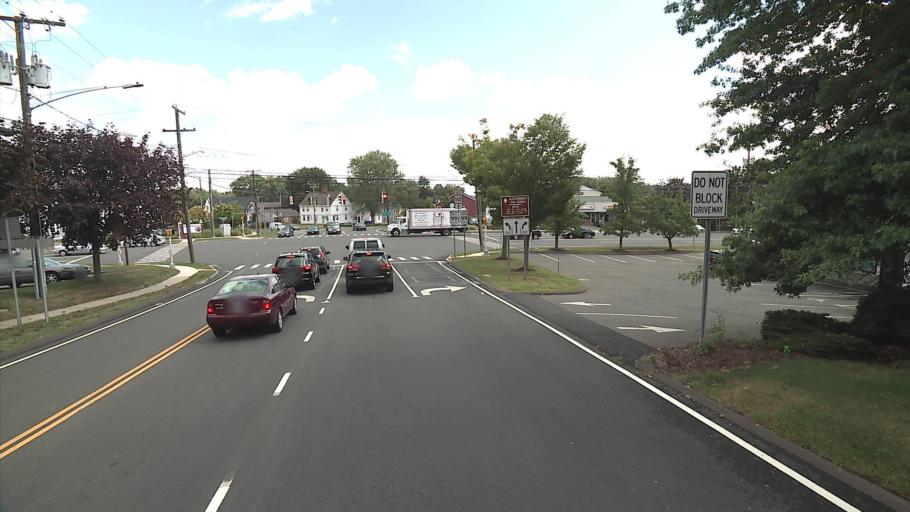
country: US
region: Connecticut
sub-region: Hartford County
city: Wethersfield
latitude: 41.6648
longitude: -72.6402
